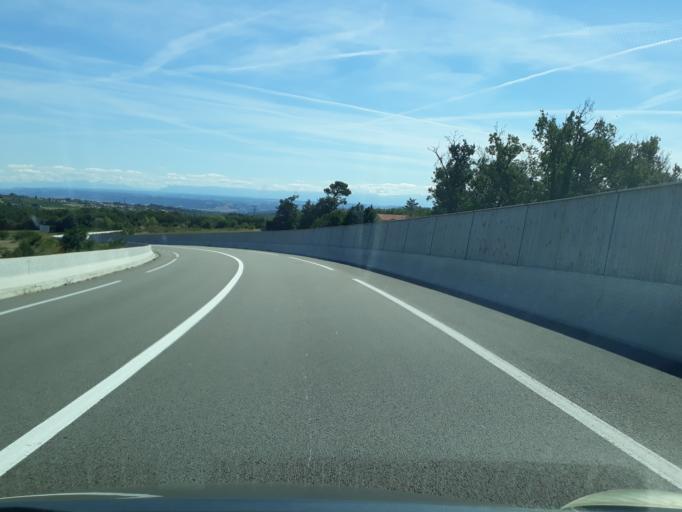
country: FR
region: Rhone-Alpes
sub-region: Departement de l'Ardeche
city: Davezieux
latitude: 45.2616
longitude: 4.7091
